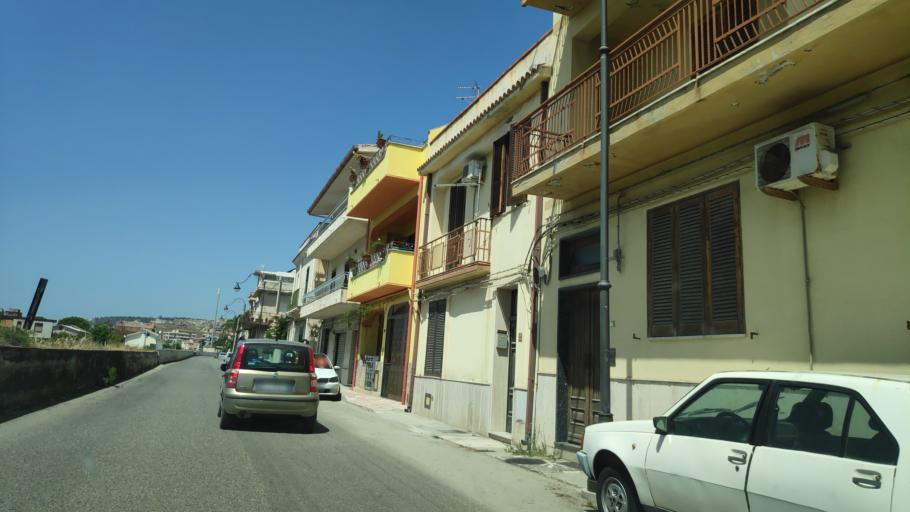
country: IT
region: Calabria
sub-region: Provincia di Reggio Calabria
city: Bova Marina
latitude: 37.9297
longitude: 15.9283
